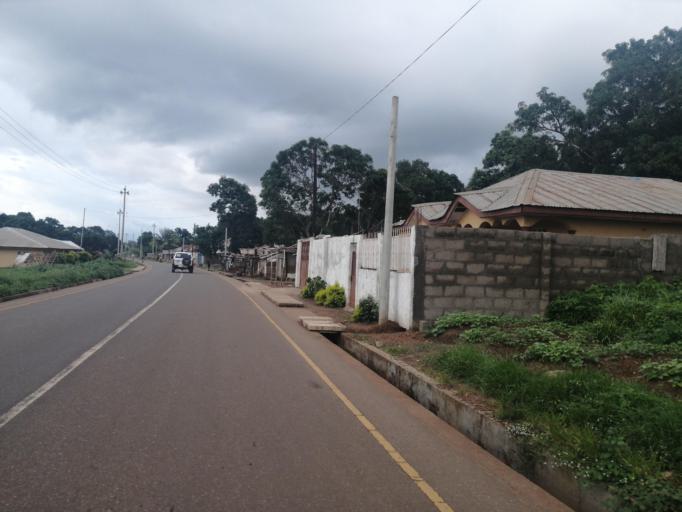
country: SL
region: Northern Province
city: Port Loko
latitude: 8.7695
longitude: -12.7795
